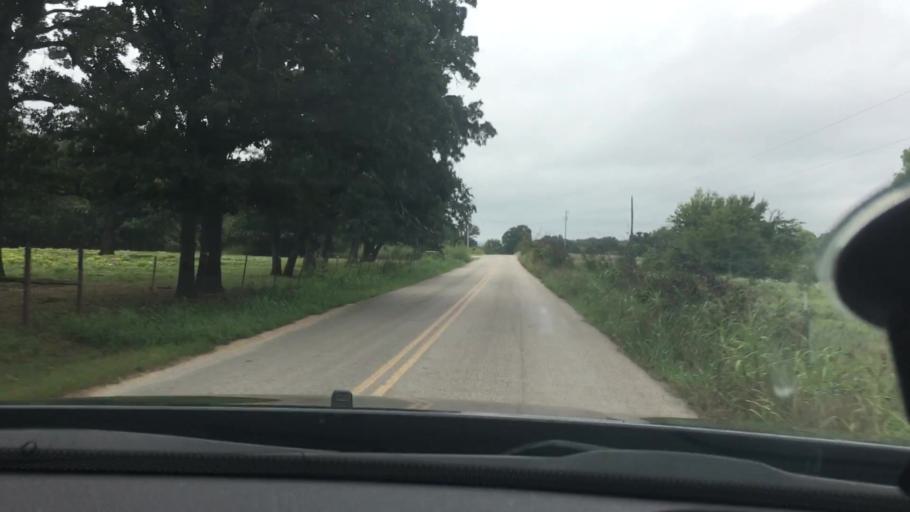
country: US
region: Oklahoma
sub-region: Pontotoc County
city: Ada
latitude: 34.8075
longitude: -96.7573
